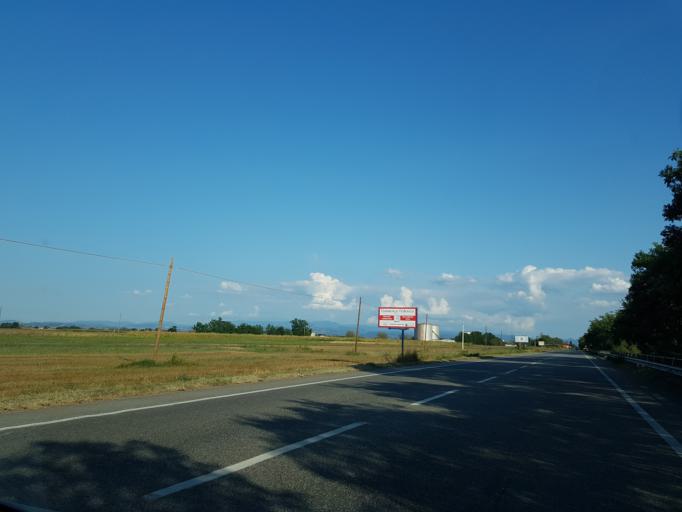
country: IT
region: Piedmont
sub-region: Provincia di Alessandria
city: Litta Parodi-Cascinagrossa
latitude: 44.8632
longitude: 8.7058
